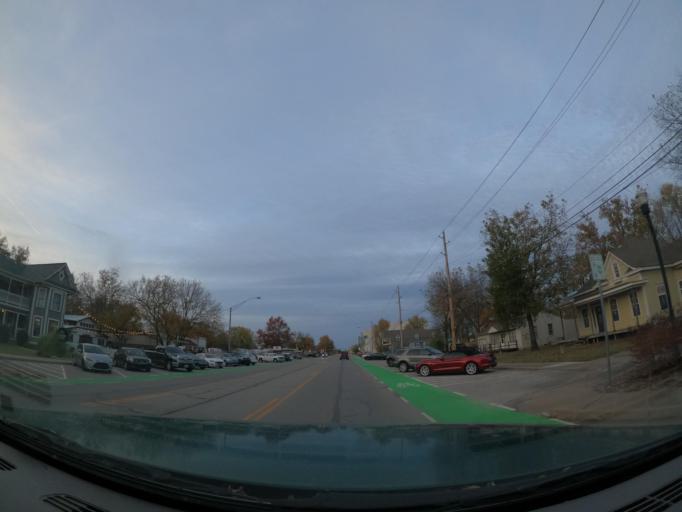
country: US
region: Oklahoma
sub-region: Tulsa County
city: Broken Arrow
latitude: 36.0435
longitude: -95.7908
